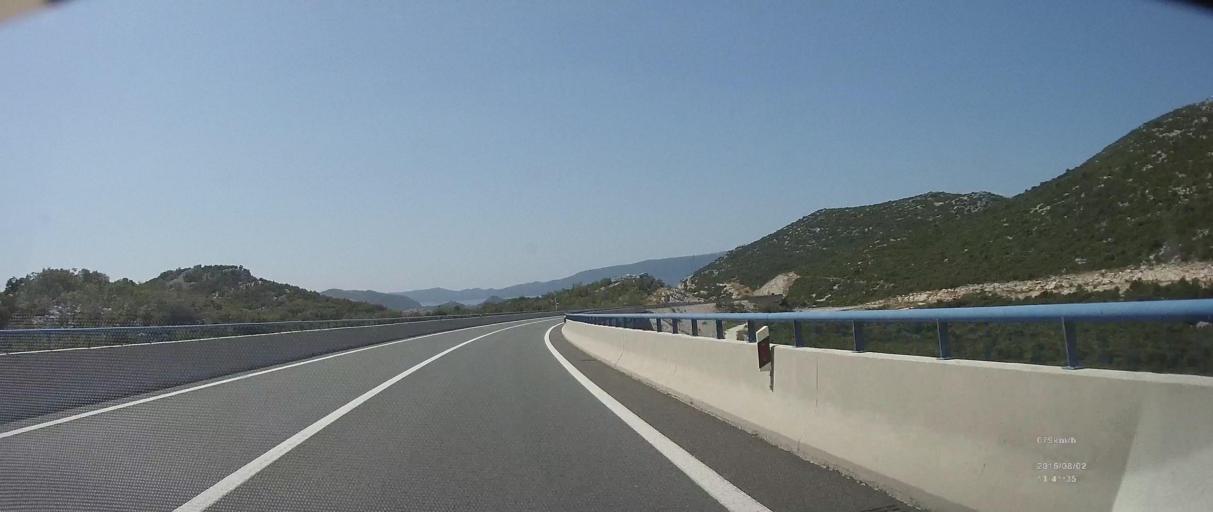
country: HR
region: Dubrovacko-Neretvanska
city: Komin
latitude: 43.0621
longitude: 17.4956
